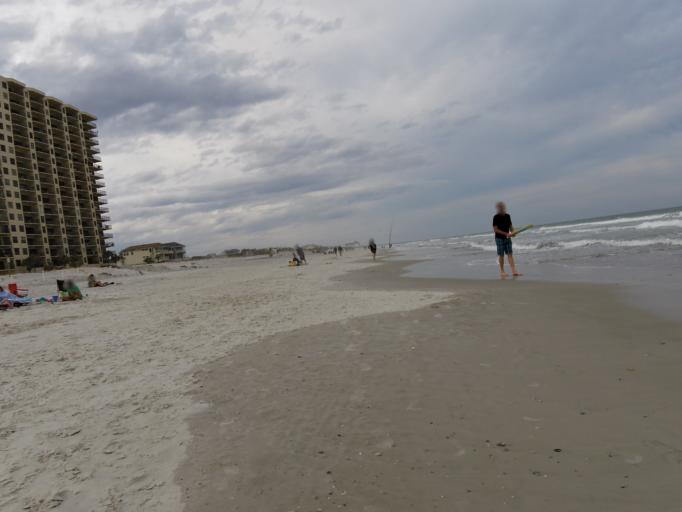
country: US
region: Florida
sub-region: Duval County
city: Neptune Beach
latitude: 30.3058
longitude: -81.3913
